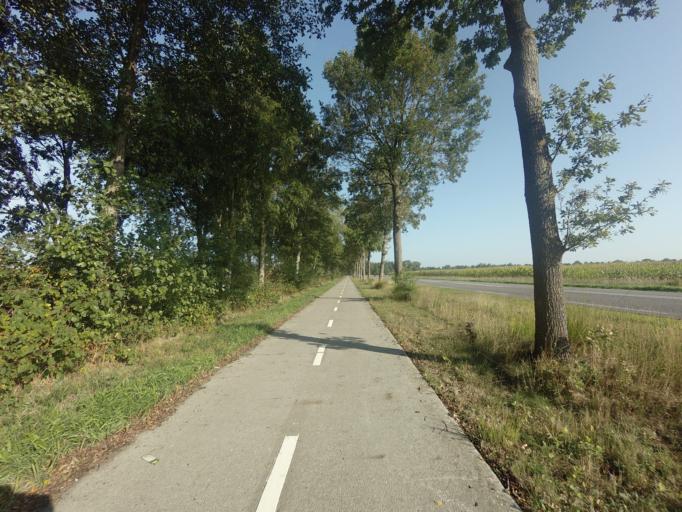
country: NL
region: Drenthe
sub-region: Gemeente Tynaarlo
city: Vries
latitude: 53.1280
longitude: 6.5011
